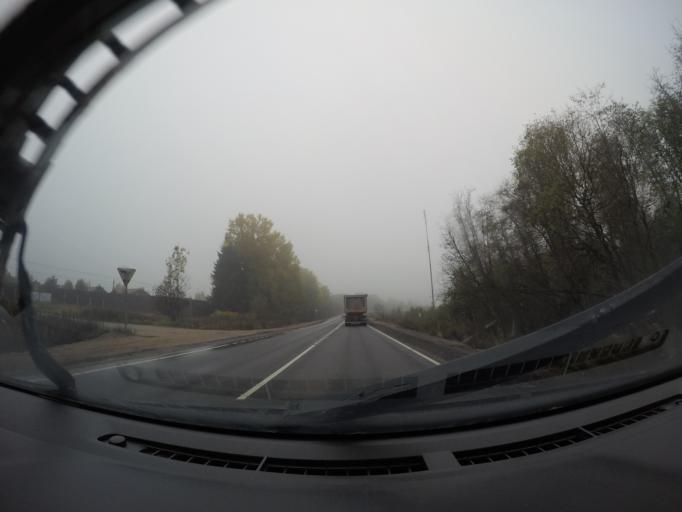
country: RU
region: Moskovskaya
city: Rumyantsevo
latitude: 55.8616
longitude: 36.5317
